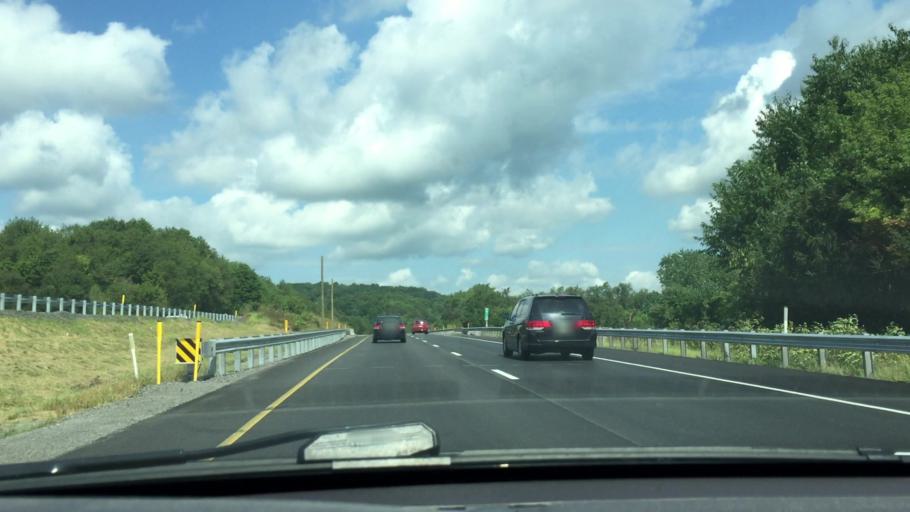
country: US
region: Pennsylvania
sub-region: Butler County
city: Zelienople
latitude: 40.8549
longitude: -80.1058
